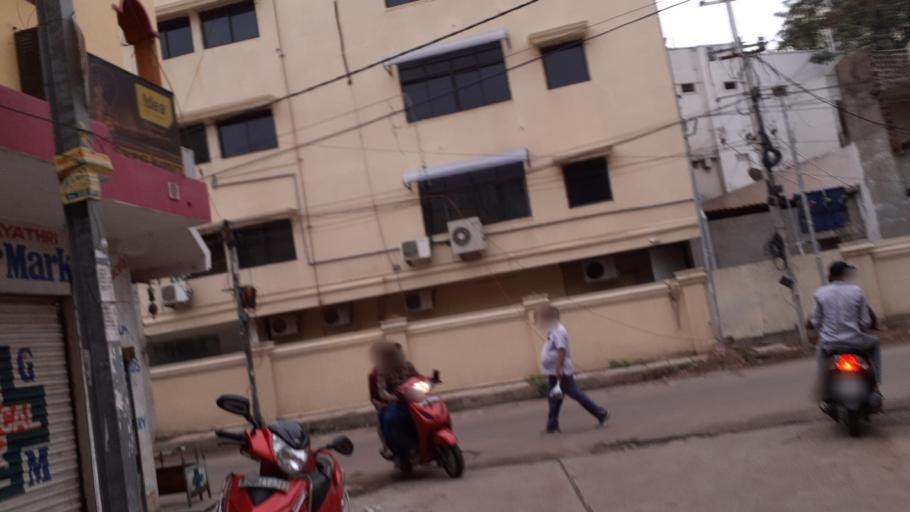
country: IN
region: Telangana
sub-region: Rangareddi
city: Kukatpalli
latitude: 17.4473
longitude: 78.4470
